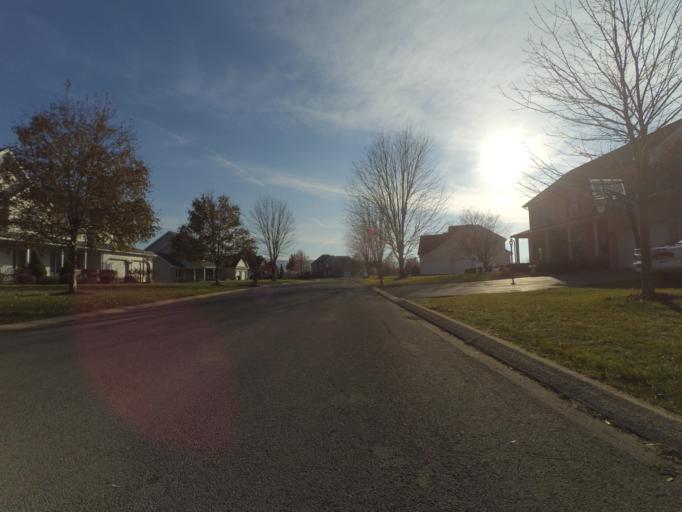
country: US
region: Pennsylvania
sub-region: Centre County
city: Lemont
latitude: 40.7985
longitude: -77.8206
